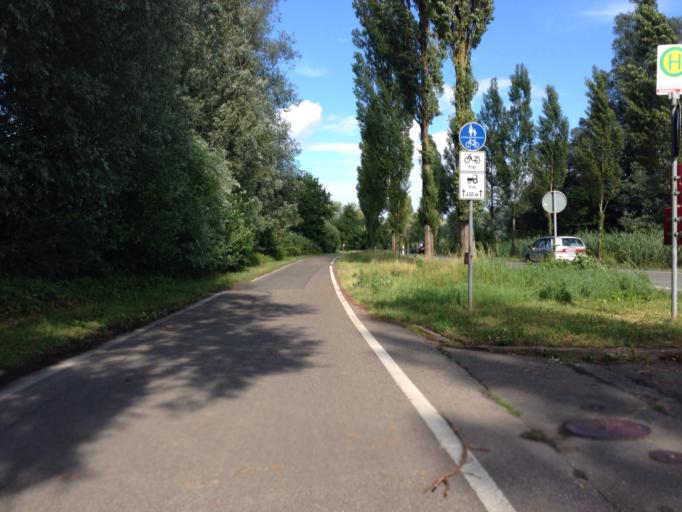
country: CH
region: Thurgau
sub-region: Kreuzlingen District
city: Ermatingen
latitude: 47.6873
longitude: 9.0928
